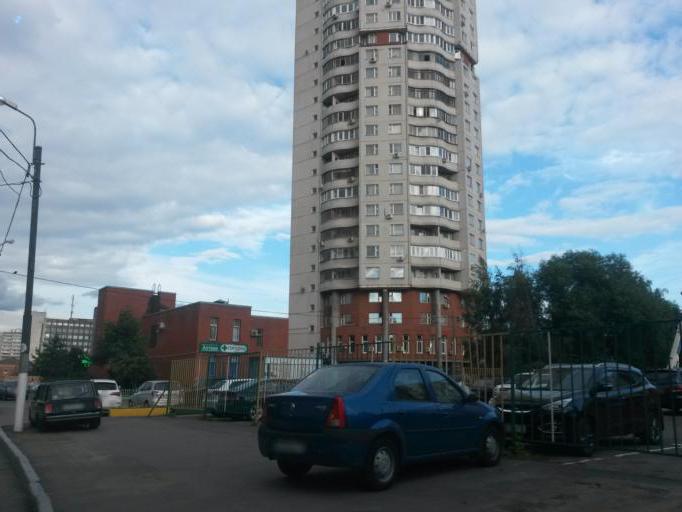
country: RU
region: Moscow
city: Orekhovo-Borisovo
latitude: 55.6063
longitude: 37.7169
